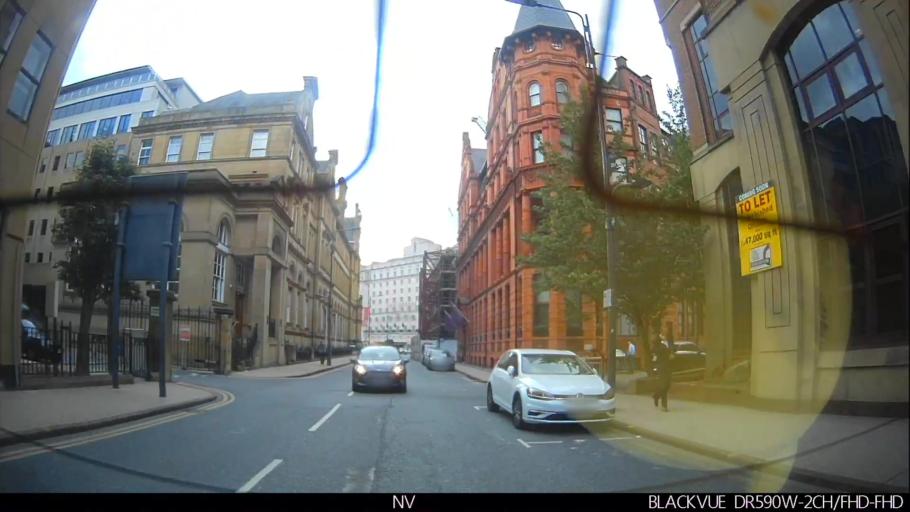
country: GB
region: England
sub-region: City and Borough of Leeds
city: Leeds
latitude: 53.7971
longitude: -1.5495
